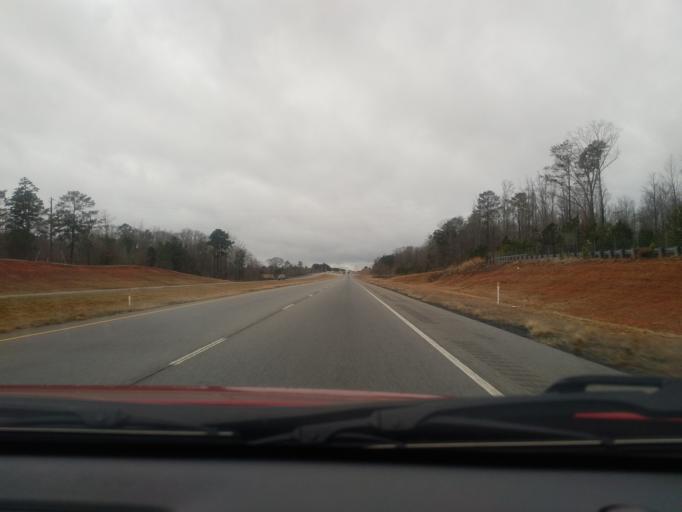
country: US
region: Georgia
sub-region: Spalding County
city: East Griffin
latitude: 33.2452
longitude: -84.1569
